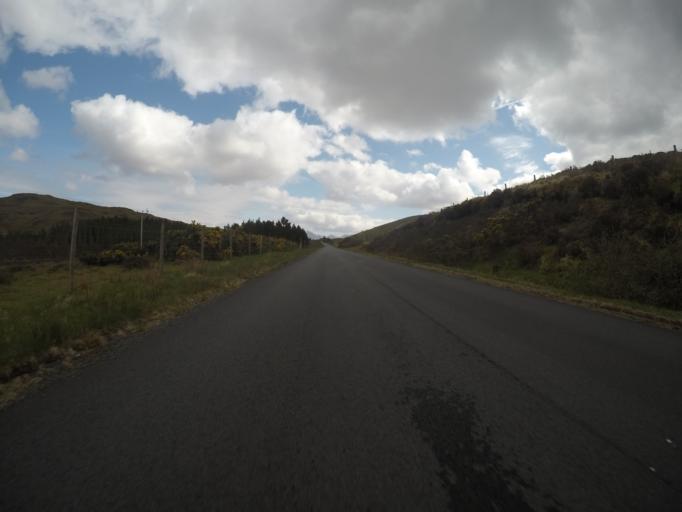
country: GB
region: Scotland
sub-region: Highland
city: Isle of Skye
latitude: 57.3365
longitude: -6.3531
